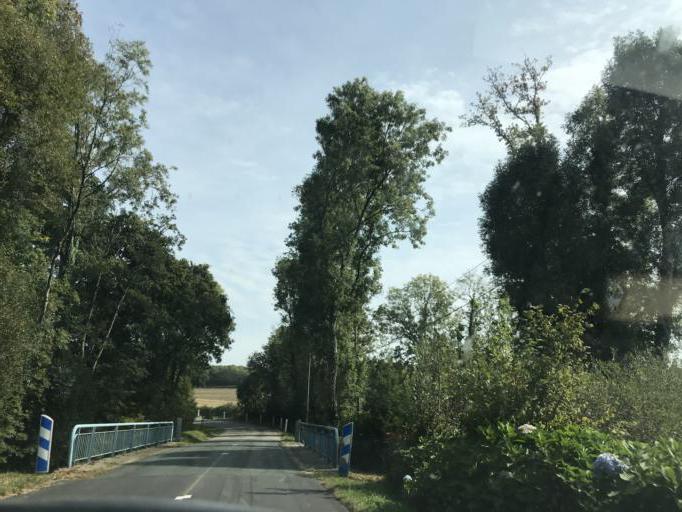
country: FR
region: Brittany
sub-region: Departement du Finistere
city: Brasparts
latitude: 48.2946
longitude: -4.0003
